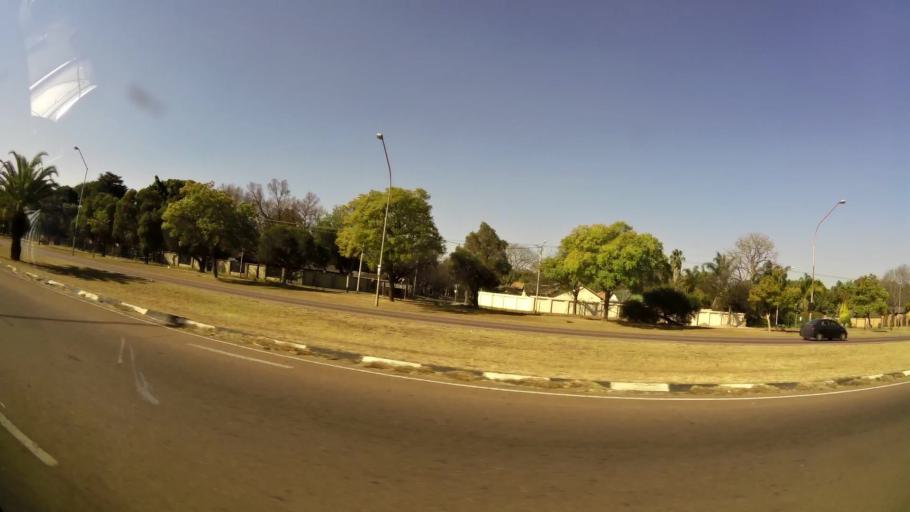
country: ZA
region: Gauteng
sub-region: City of Tshwane Metropolitan Municipality
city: Pretoria
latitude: -25.7290
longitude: 28.2584
